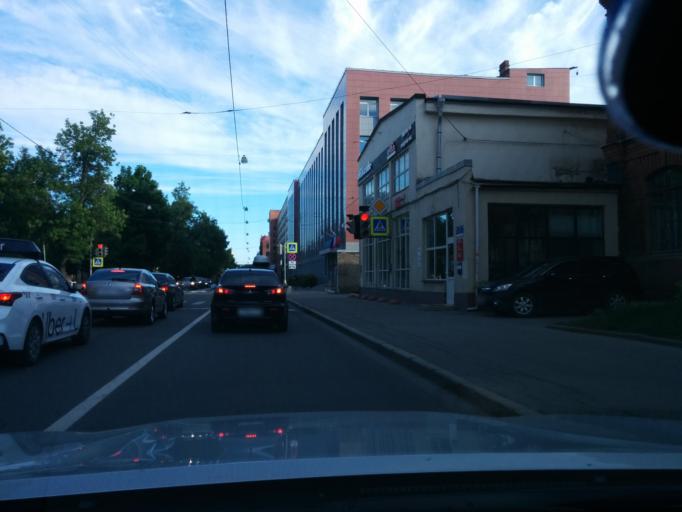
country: RU
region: Leningrad
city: Sampsonievskiy
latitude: 59.9774
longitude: 30.3380
